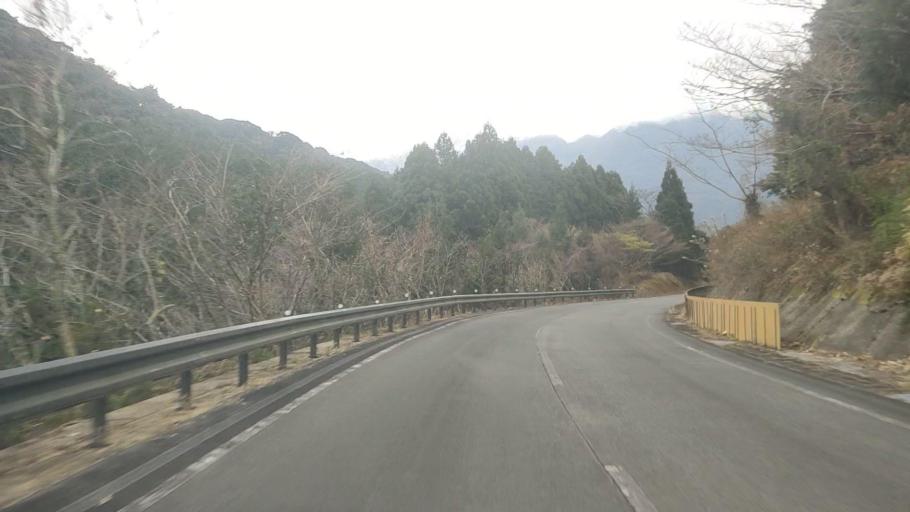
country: JP
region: Nagasaki
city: Shimabara
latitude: 32.7885
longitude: 130.2833
